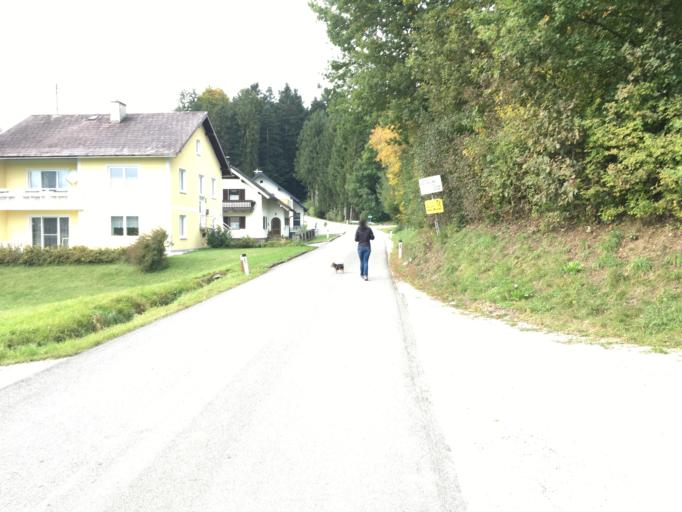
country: AT
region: Upper Austria
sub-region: Politischer Bezirk Vocklabruck
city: Pfaffing
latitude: 48.0046
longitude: 13.4633
